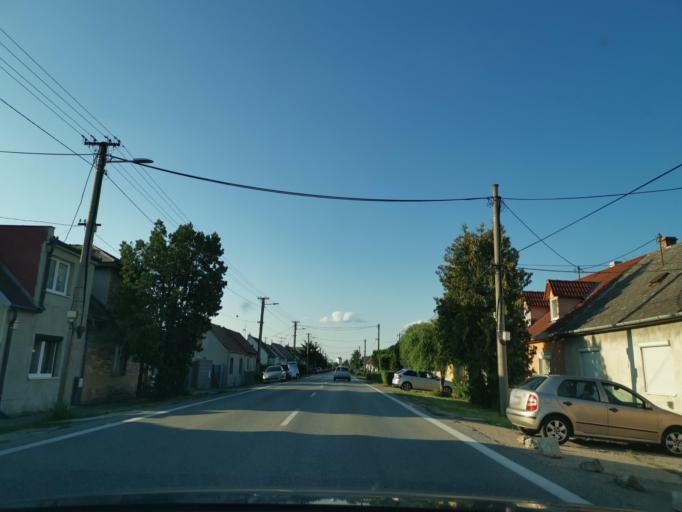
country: SK
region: Bratislavsky
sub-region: Okres Malacky
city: Malacky
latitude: 48.4208
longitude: 17.0201
